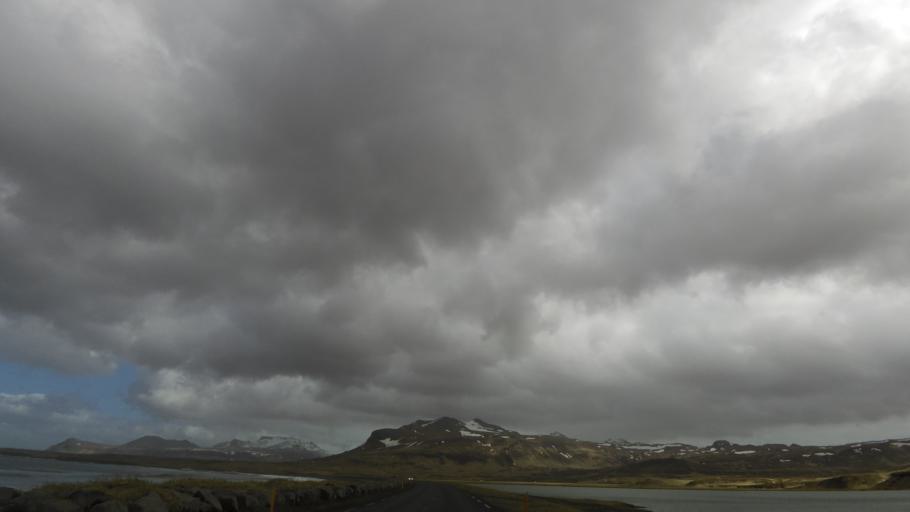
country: IS
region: West
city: Olafsvik
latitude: 64.8892
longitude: -23.6423
